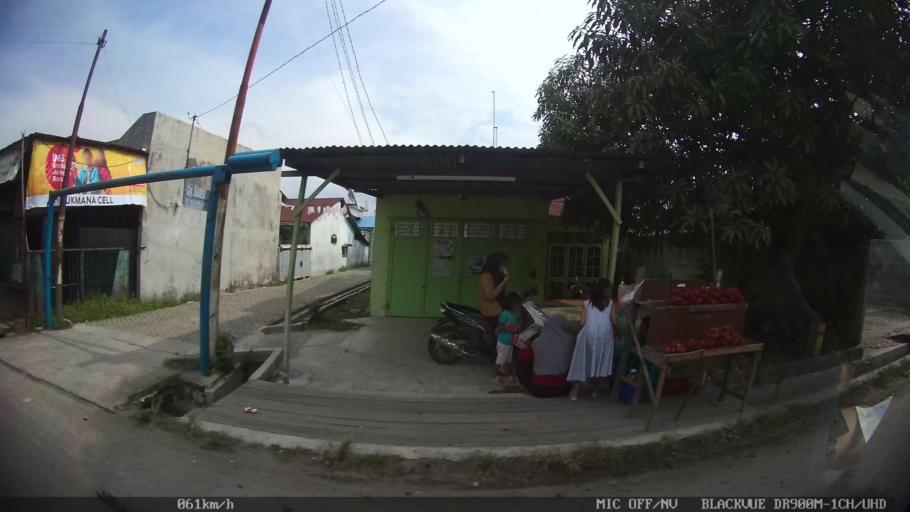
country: ID
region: North Sumatra
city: Percut
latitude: 3.6071
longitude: 98.7746
